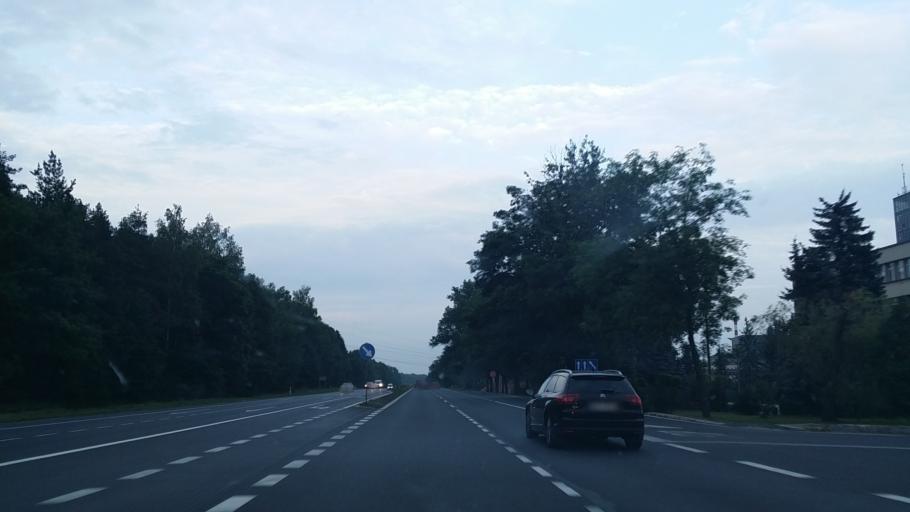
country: PL
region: Lower Silesian Voivodeship
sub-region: Powiat lubinski
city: Lubin
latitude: 51.4355
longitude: 16.1584
